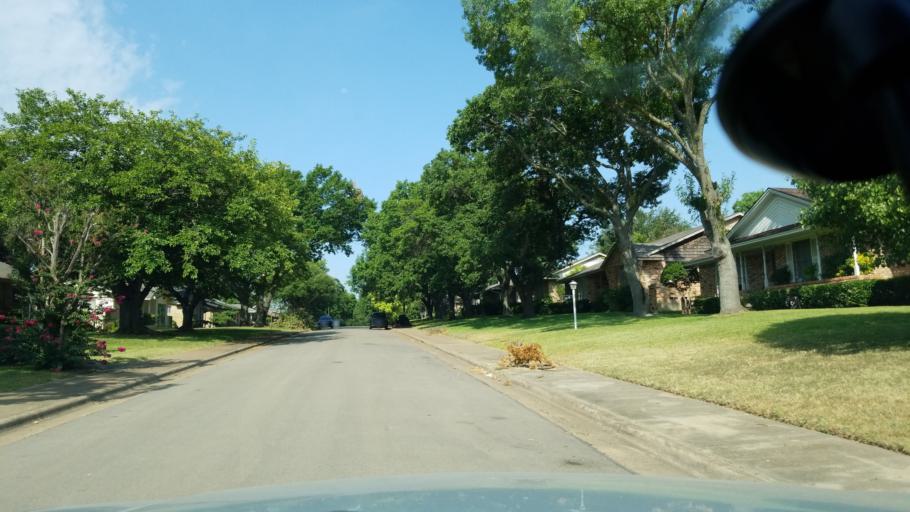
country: US
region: Texas
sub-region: Dallas County
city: Duncanville
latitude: 32.6737
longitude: -96.8460
